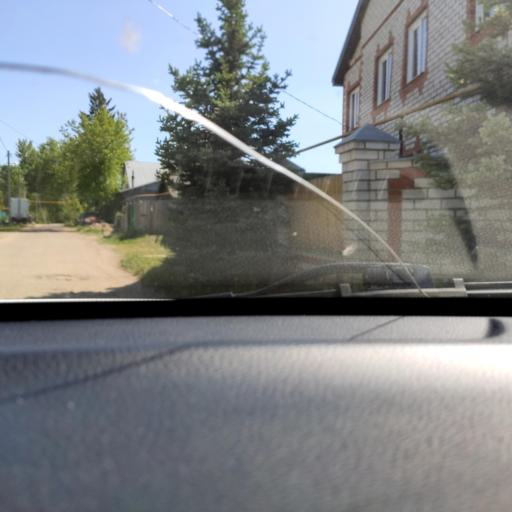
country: RU
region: Tatarstan
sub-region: Gorod Kazan'
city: Kazan
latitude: 55.8597
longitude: 49.1984
